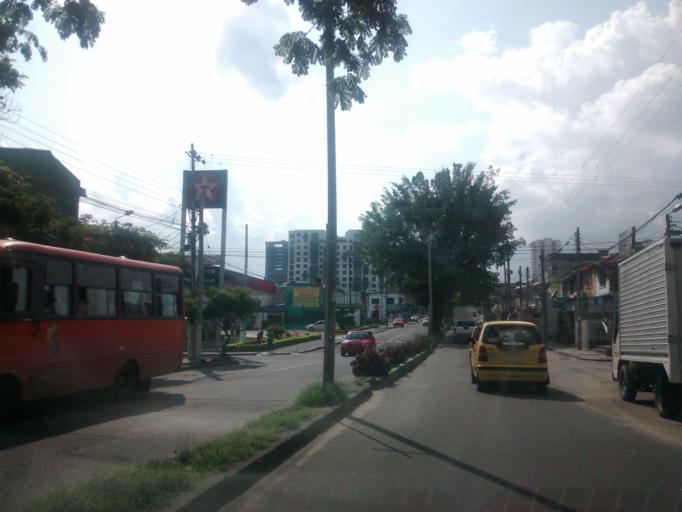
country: CO
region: Tolima
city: Ibague
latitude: 4.4422
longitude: -75.1992
